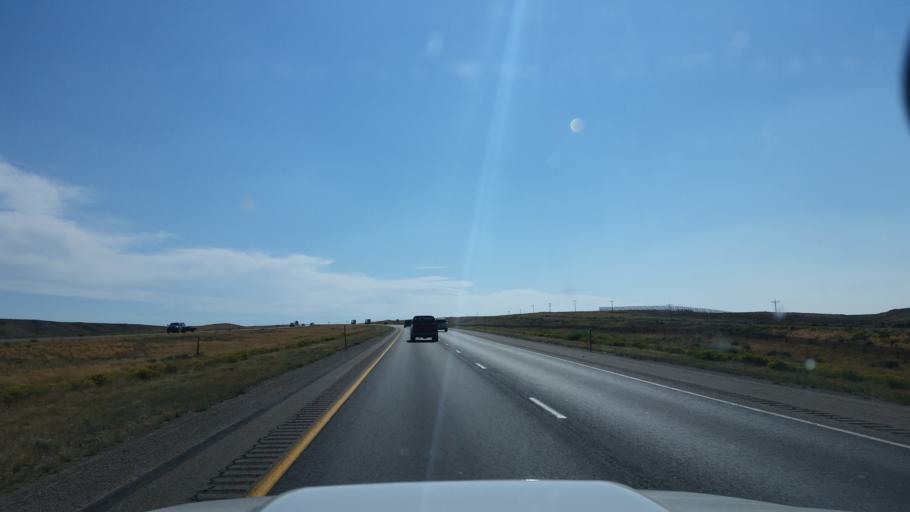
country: US
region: Wyoming
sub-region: Uinta County
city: Lyman
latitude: 41.5017
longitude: -110.0018
